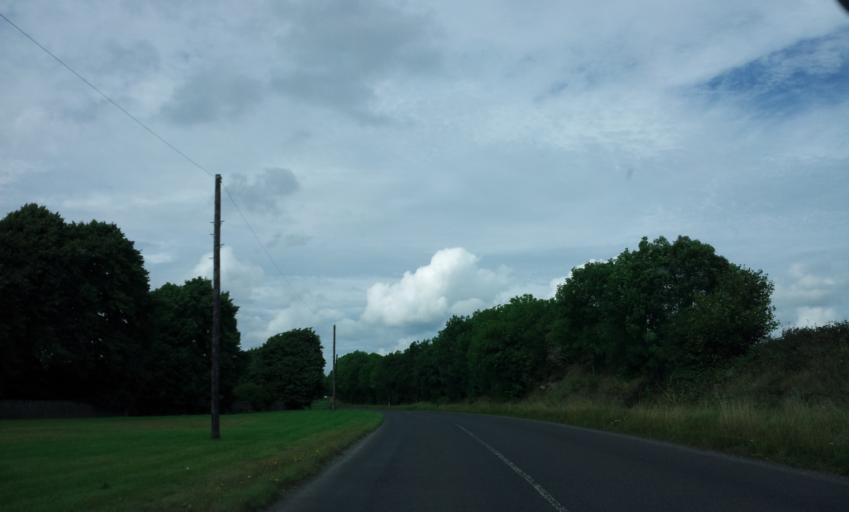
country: IE
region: Leinster
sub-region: Laois
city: Stradbally
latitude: 53.0041
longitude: -7.2273
